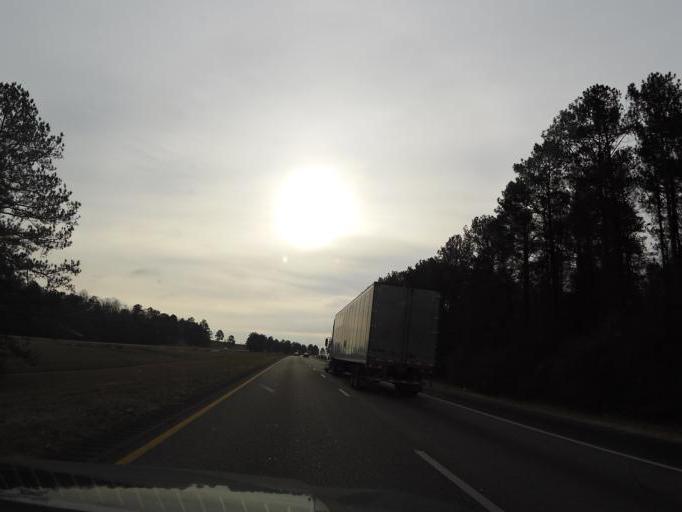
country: US
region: Alabama
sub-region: Autauga County
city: Prattville
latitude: 32.5142
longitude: -86.4305
